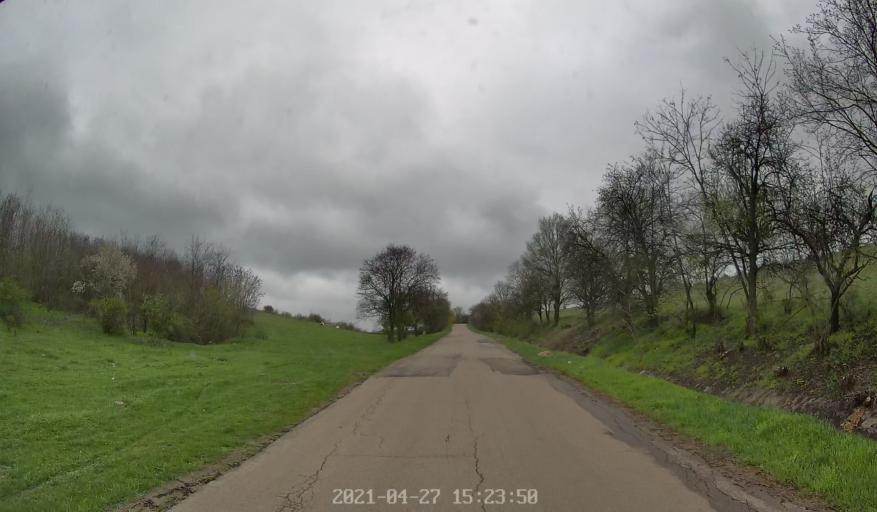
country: MD
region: Chisinau
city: Vadul lui Voda
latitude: 47.0183
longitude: 29.0248
